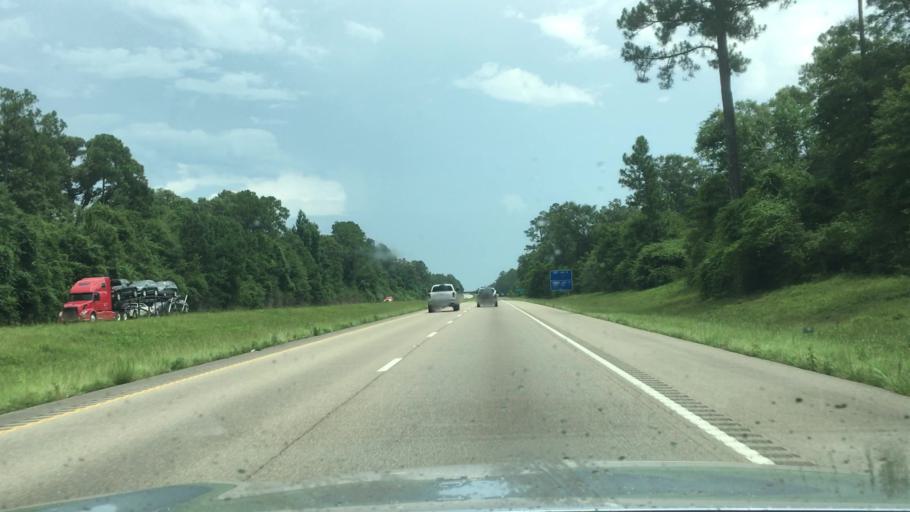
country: US
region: Mississippi
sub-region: Lamar County
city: Lumberton
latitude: 30.9165
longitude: -89.4625
